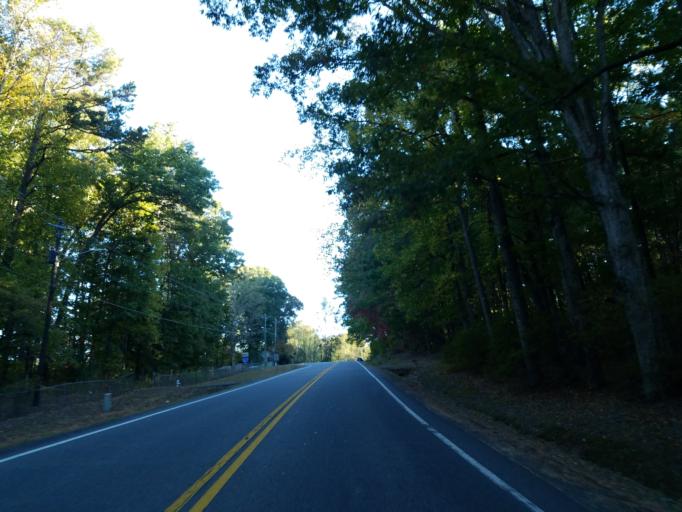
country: US
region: Georgia
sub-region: Dawson County
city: Dawsonville
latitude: 34.4136
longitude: -84.1171
